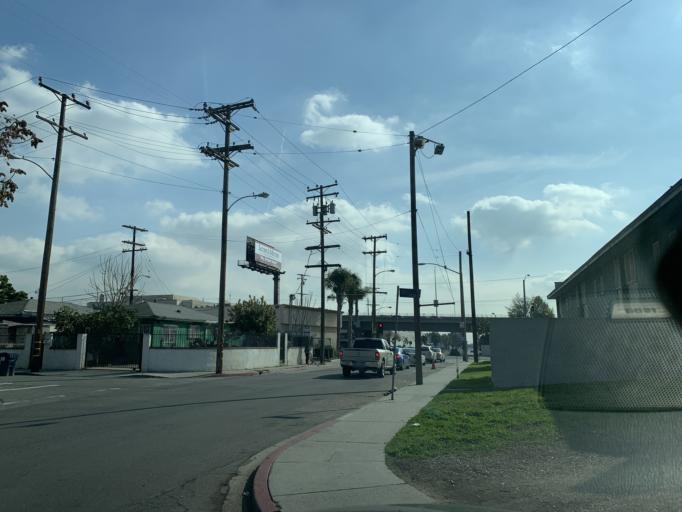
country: US
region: California
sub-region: Los Angeles County
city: Lynwood
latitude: 33.9298
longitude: -118.2305
